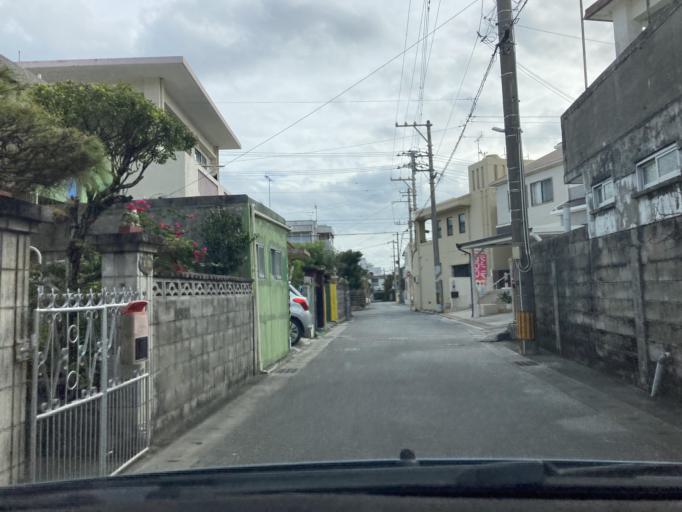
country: JP
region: Okinawa
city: Ginowan
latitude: 26.2028
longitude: 127.7526
